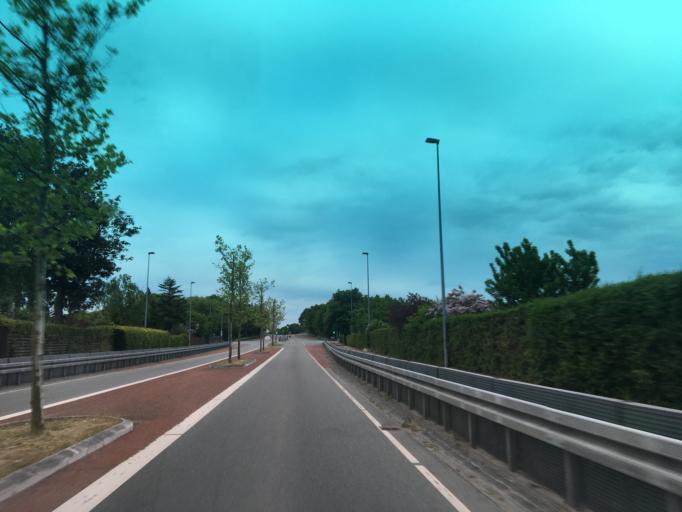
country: DK
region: Capital Region
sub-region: Albertslund Kommune
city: Albertslund
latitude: 55.6448
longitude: 12.3558
